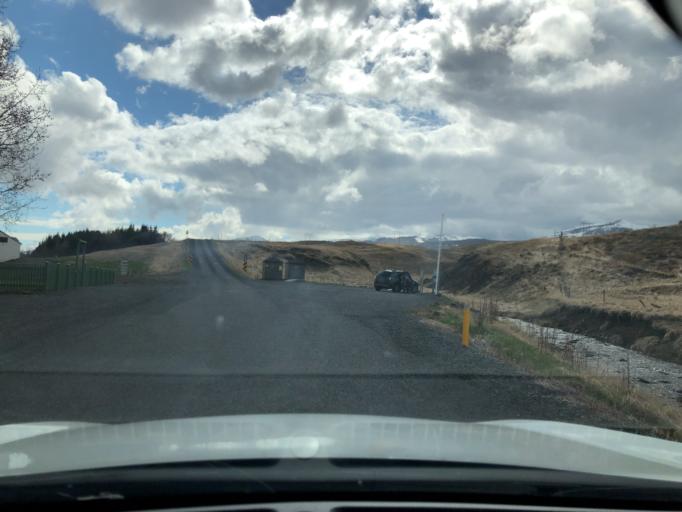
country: IS
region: Northwest
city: Saudarkrokur
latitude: 65.5391
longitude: -19.4713
